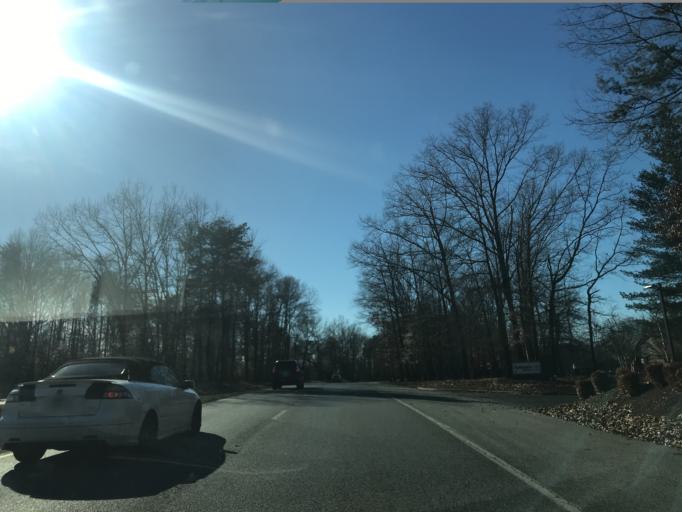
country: US
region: Maryland
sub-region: Charles County
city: Saint Charles
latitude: 38.6061
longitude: -76.8914
